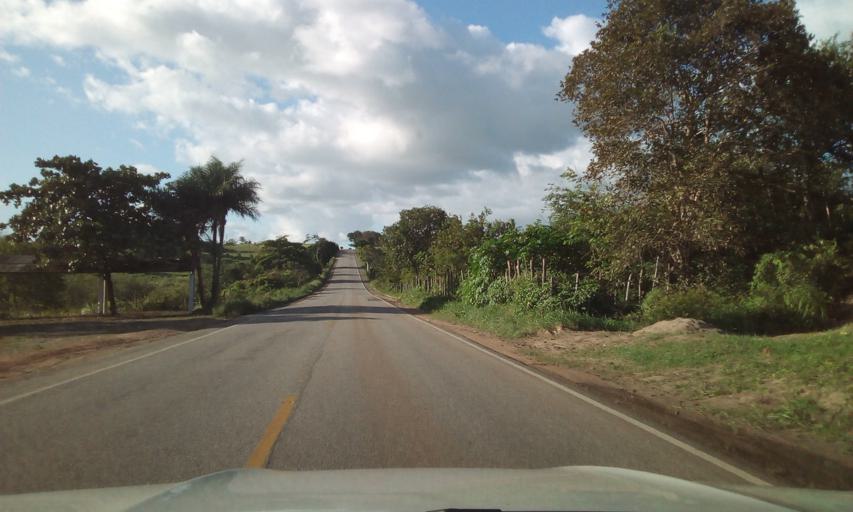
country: BR
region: Paraiba
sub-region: Pilar
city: Pilar
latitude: -7.1832
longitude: -35.2307
